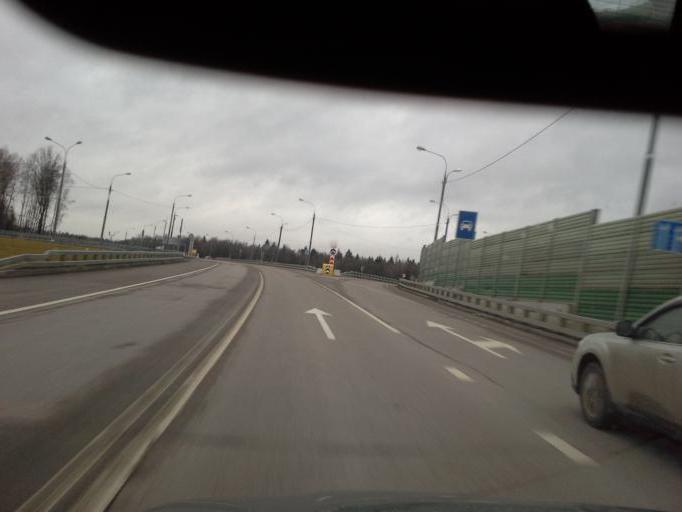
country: RU
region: Moskovskaya
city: Kokoshkino
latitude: 55.6216
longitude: 37.1550
